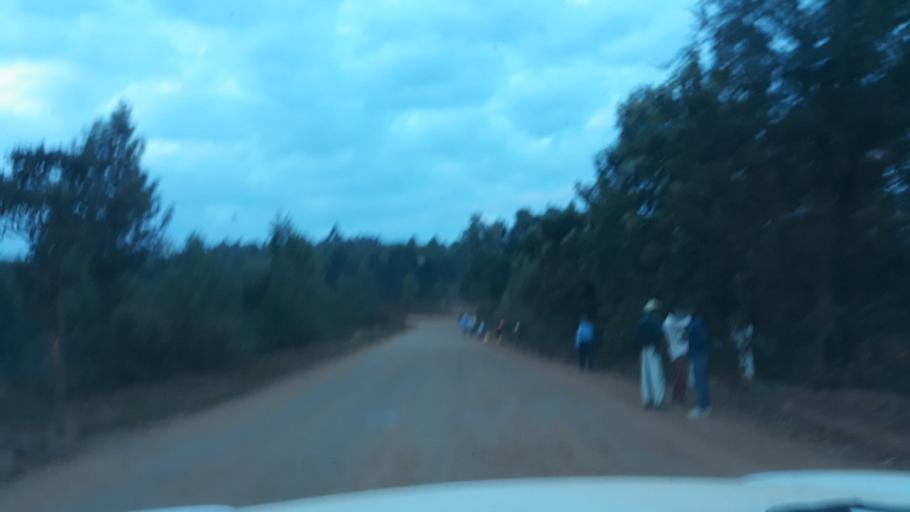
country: CD
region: South Kivu
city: Bukavu
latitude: -2.5864
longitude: 28.8552
